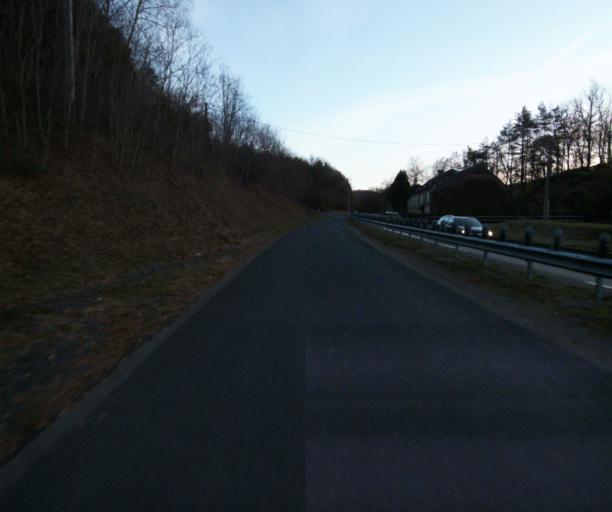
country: FR
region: Limousin
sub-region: Departement de la Correze
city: Laguenne
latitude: 45.2297
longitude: 1.8107
